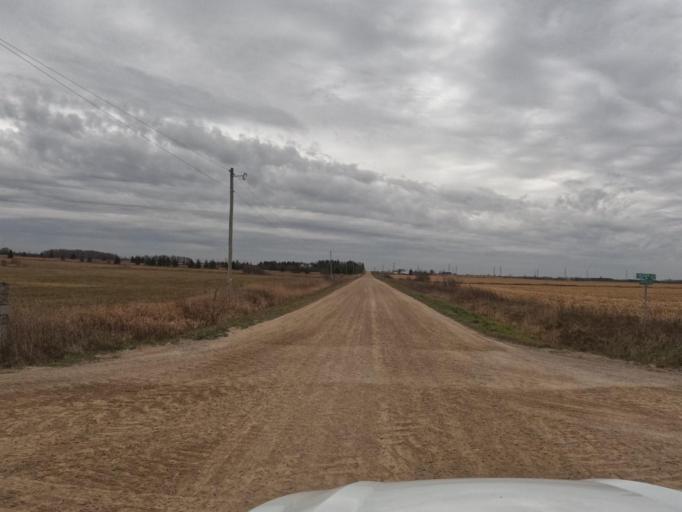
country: CA
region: Ontario
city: Shelburne
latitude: 44.0108
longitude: -80.3895
